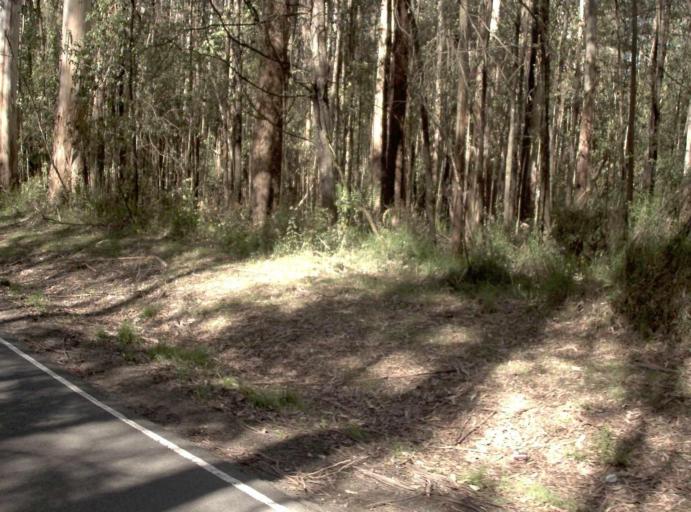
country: AU
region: Victoria
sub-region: Yarra Ranges
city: Millgrove
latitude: -37.8721
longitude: 145.8029
